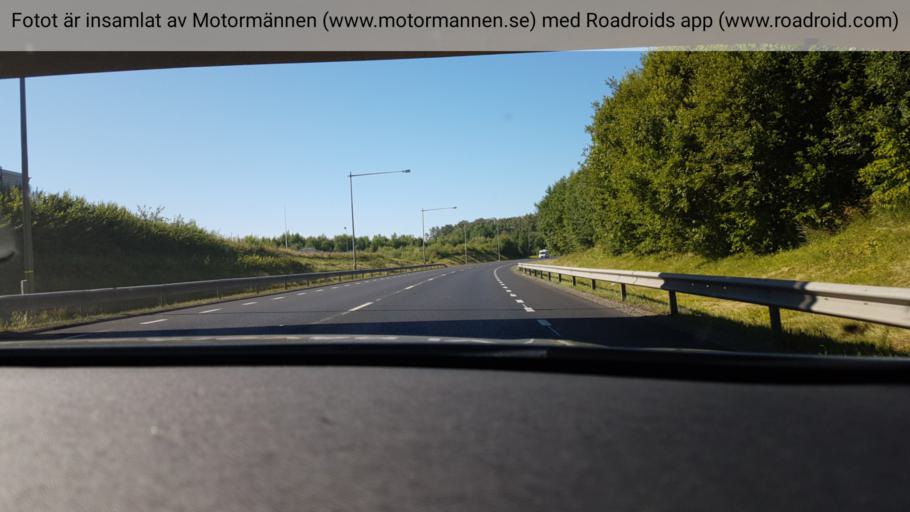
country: SE
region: Vaestra Goetaland
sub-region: Skovde Kommun
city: Skoevde
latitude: 58.3864
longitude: 13.8748
